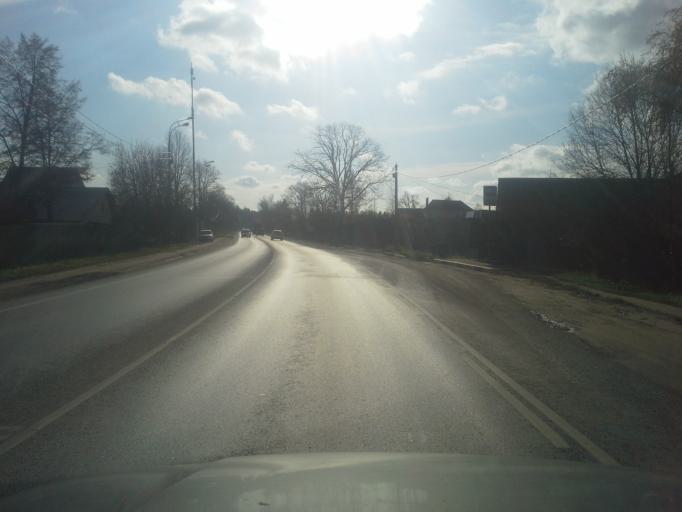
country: RU
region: Moskovskaya
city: Bol'shiye Vyazemy
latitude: 55.6648
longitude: 36.9638
